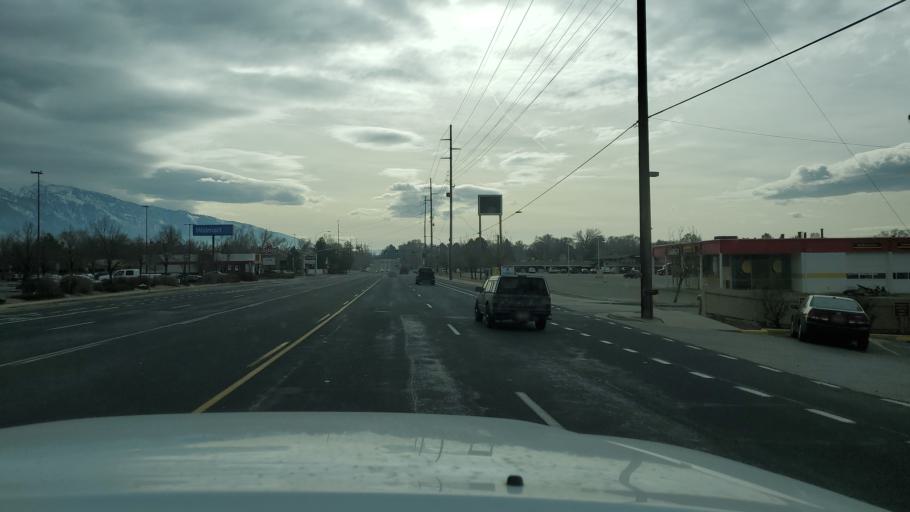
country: US
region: Utah
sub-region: Salt Lake County
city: Millcreek
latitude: 40.6699
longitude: -111.8654
